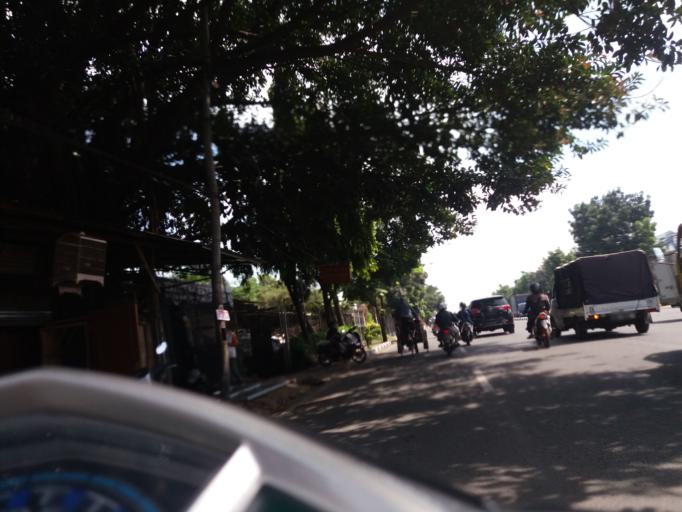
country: ID
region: West Java
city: Margahayukencana
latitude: -6.9478
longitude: 107.5997
